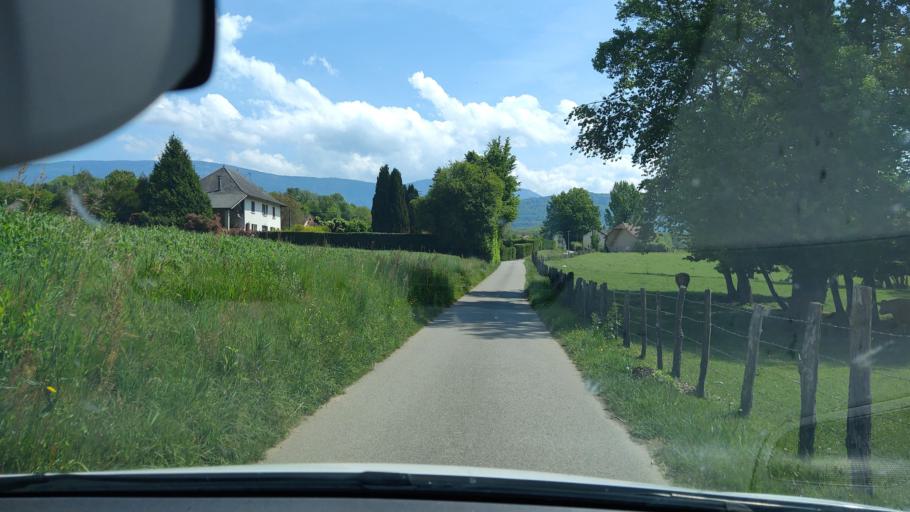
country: FR
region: Rhone-Alpes
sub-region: Departement de la Savoie
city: Domessin
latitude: 45.5286
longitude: 5.7100
